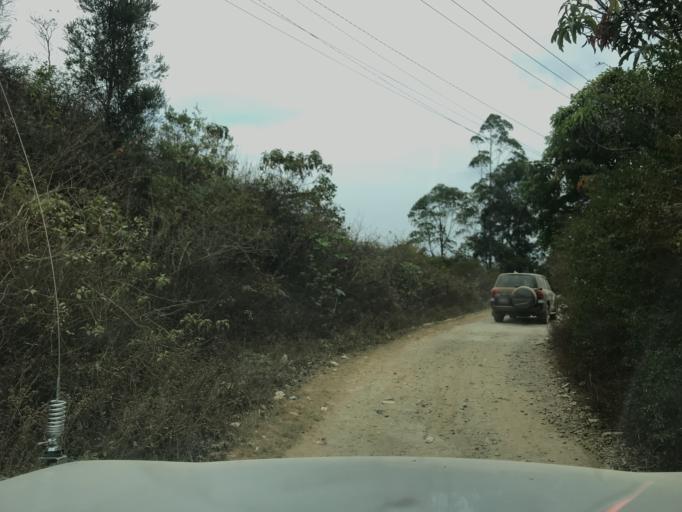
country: TL
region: Ermera
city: Gleno
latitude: -8.8378
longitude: 125.4351
